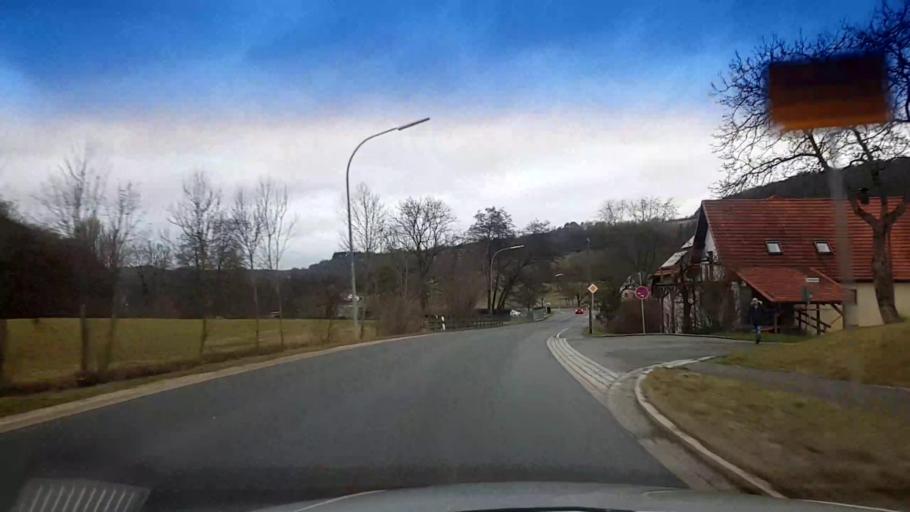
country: DE
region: Bavaria
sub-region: Upper Franconia
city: Wattendorf
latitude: 50.0635
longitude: 11.0712
